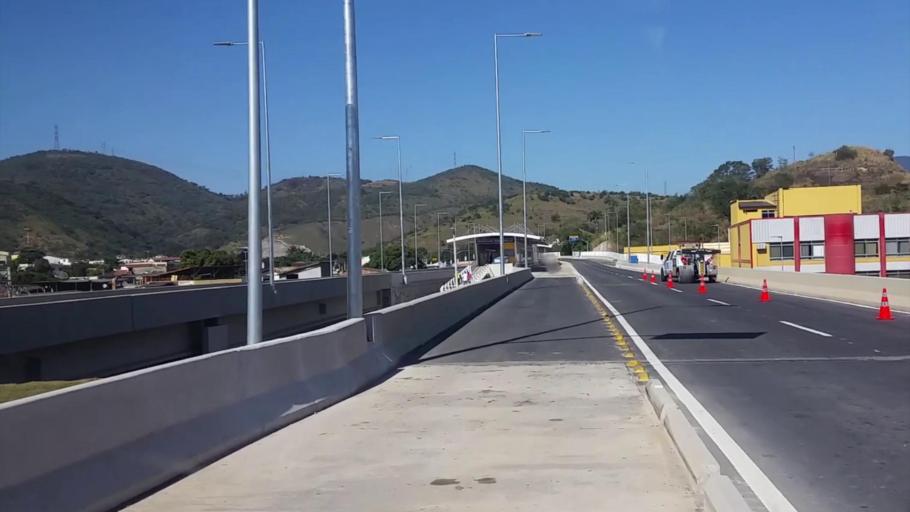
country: BR
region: Rio de Janeiro
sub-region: Nilopolis
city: Nilopolis
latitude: -22.8773
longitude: -43.4038
